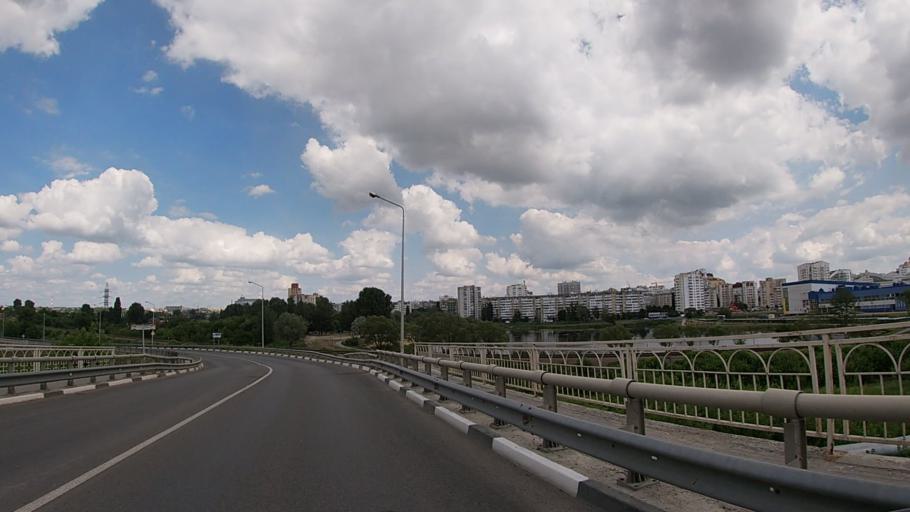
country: RU
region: Belgorod
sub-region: Belgorodskiy Rayon
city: Belgorod
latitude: 50.5904
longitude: 36.5657
